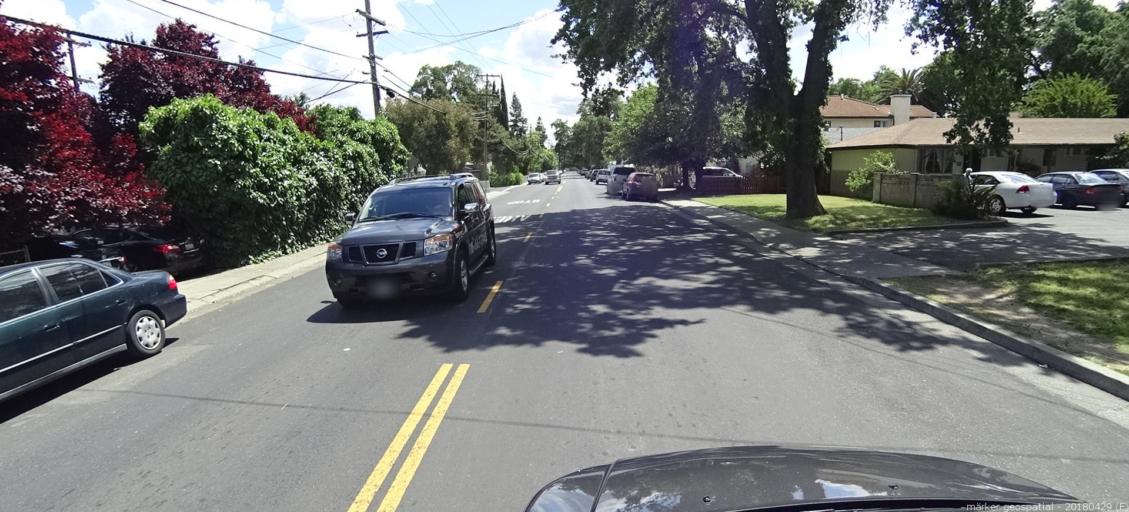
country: US
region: California
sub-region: Yolo County
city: West Sacramento
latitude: 38.5955
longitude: -121.5388
